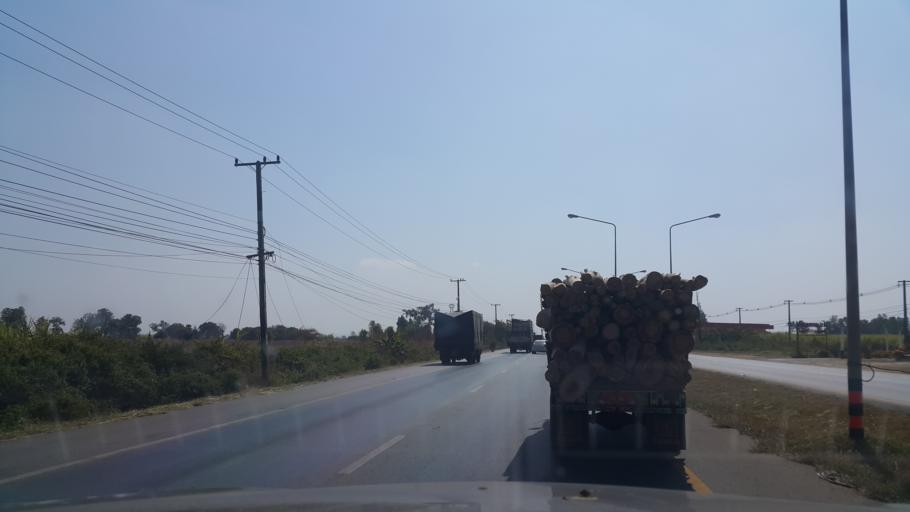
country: TH
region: Changwat Udon Thani
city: Non Sa-at
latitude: 16.9948
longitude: 102.8932
